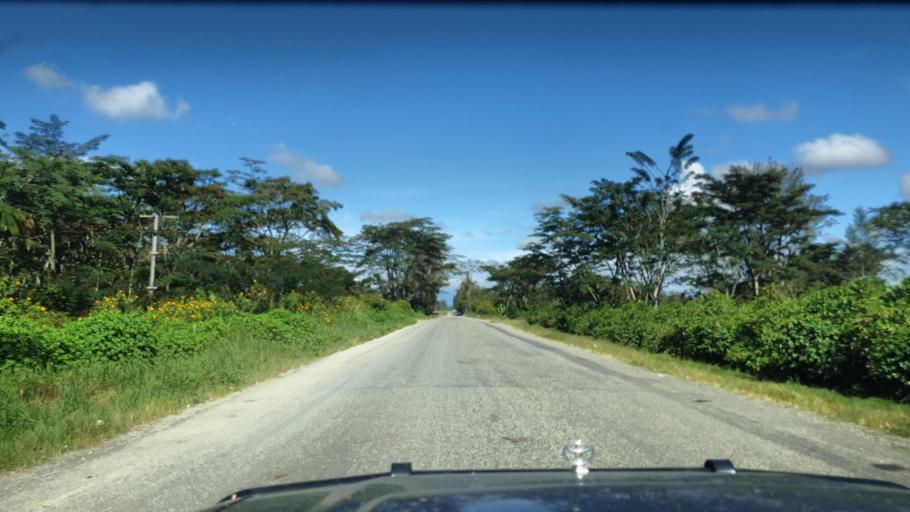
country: PG
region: Western Highlands
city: Rauna
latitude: -5.8338
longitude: 144.3449
